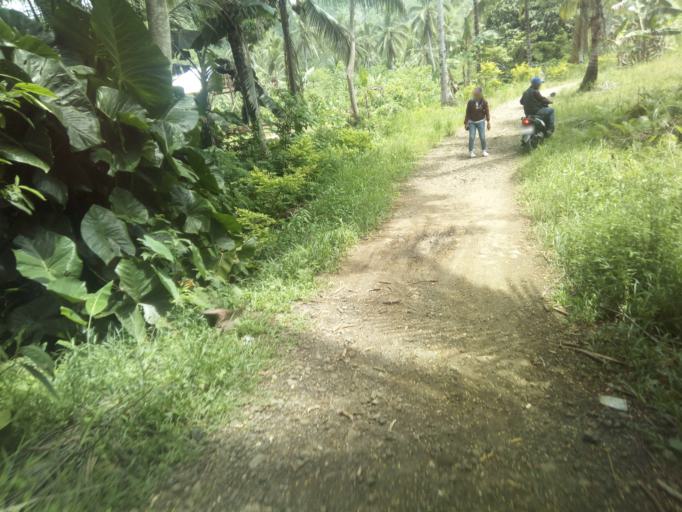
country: PH
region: Caraga
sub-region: Province of Agusan del Sur
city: Santa Josefa
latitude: 7.9542
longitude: 125.9837
